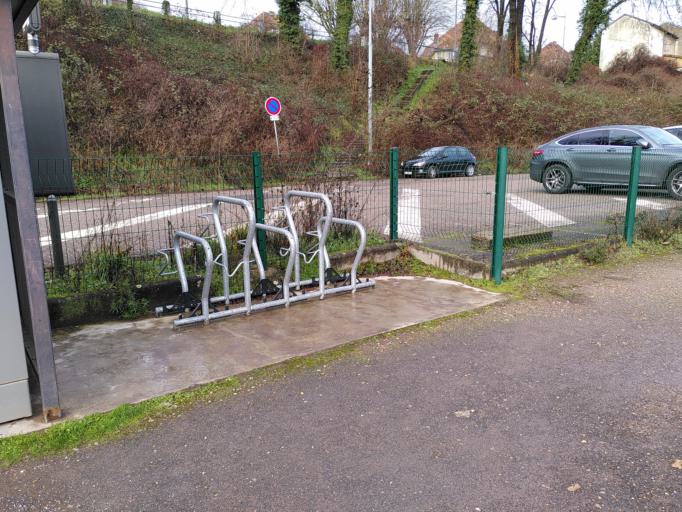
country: FR
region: Lorraine
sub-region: Departement de Meurthe-et-Moselle
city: Pompey
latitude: 48.7730
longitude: 6.1307
